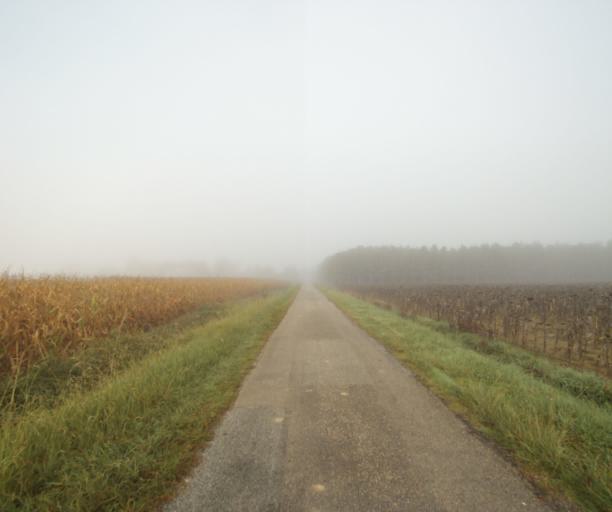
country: FR
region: Midi-Pyrenees
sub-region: Departement du Tarn-et-Garonne
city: Nohic
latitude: 43.8942
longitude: 1.4487
